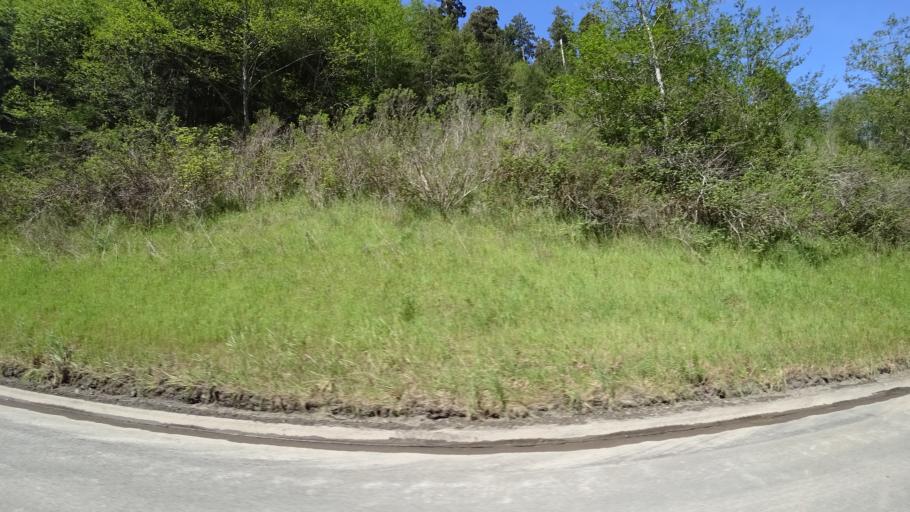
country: US
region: California
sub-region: Del Norte County
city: Bertsch-Oceanview
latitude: 41.4566
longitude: -124.0313
